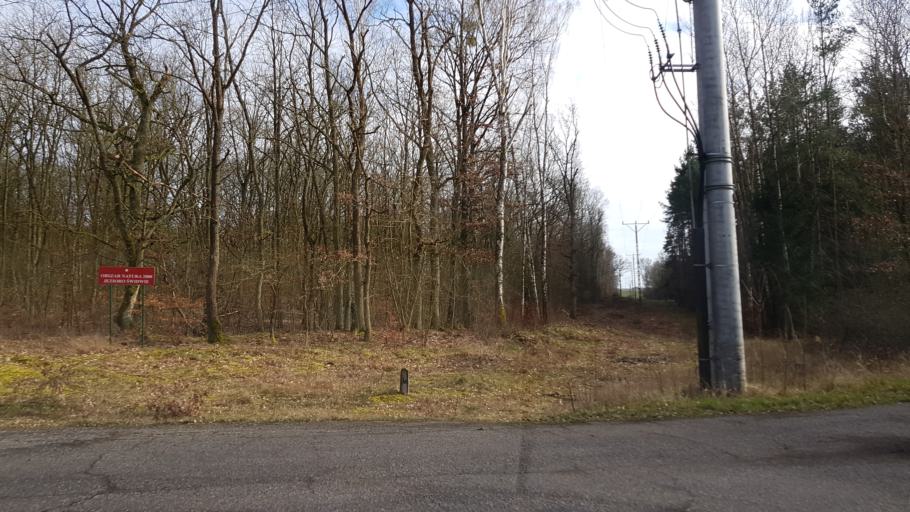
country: PL
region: West Pomeranian Voivodeship
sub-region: Powiat policki
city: Dobra
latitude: 53.5266
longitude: 14.3226
